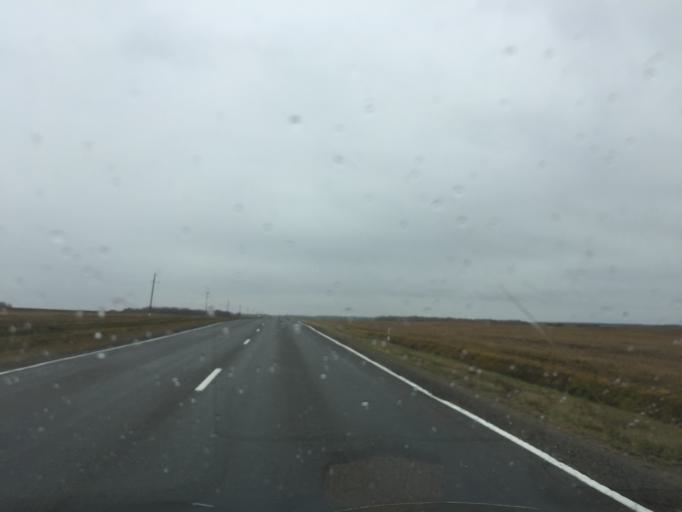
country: BY
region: Mogilev
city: Cherykaw
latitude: 53.6041
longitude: 31.3211
